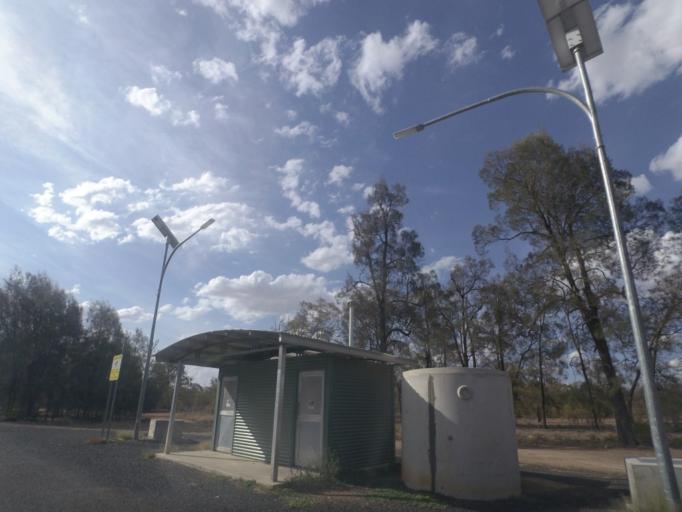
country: AU
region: New South Wales
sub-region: Moree Plains
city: Boggabilla
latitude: -28.4882
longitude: 150.4846
